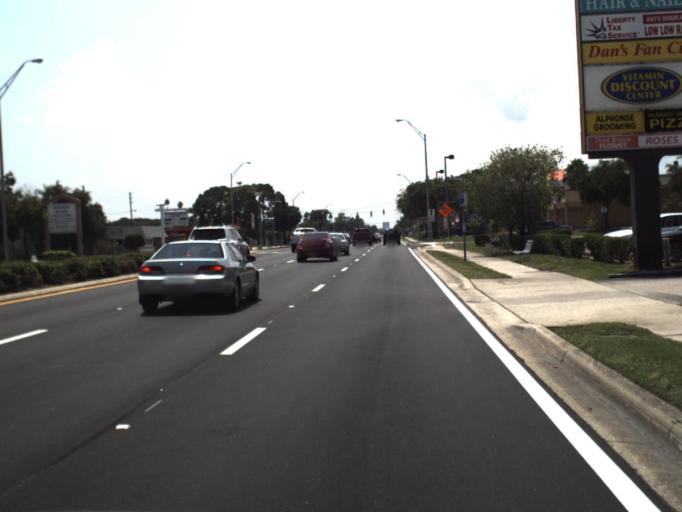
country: US
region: Florida
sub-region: Pinellas County
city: Lealman
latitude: 27.8233
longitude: -82.6388
